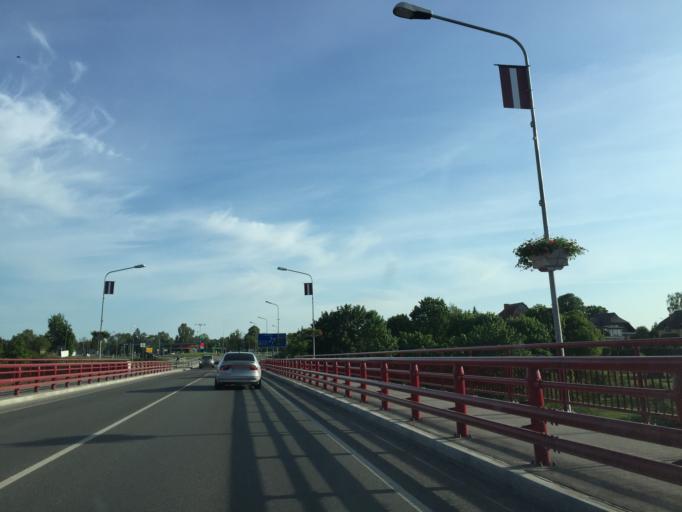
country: LV
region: Bauskas Rajons
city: Bauska
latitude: 56.4018
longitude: 24.1778
